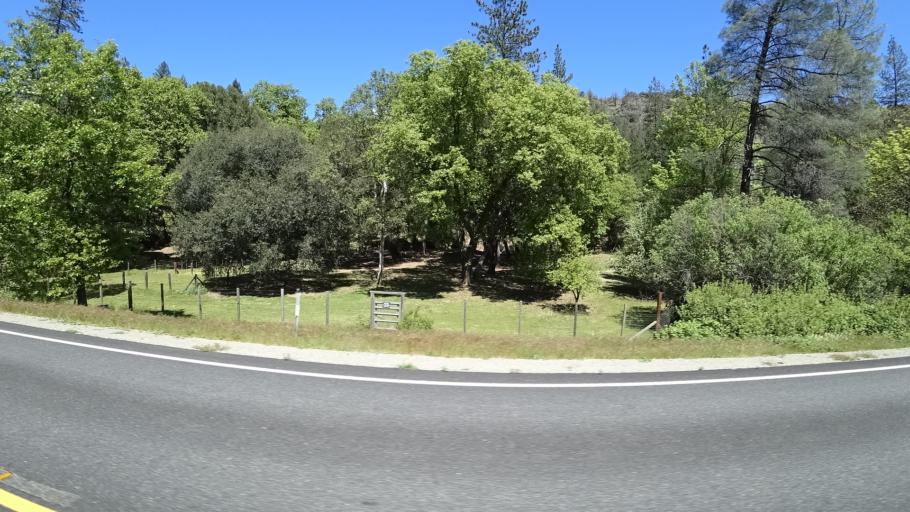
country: US
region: California
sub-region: Trinity County
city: Weaverville
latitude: 40.7424
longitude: -123.0642
